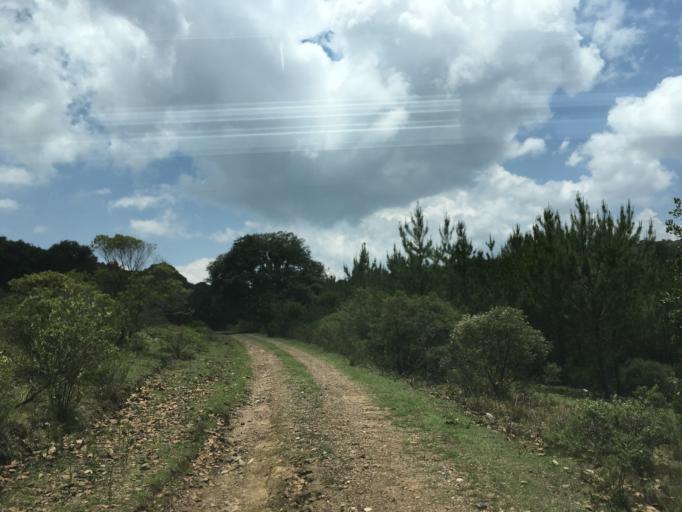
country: MX
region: Oaxaca
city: San Andres Sinaxtla
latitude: 17.6078
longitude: -97.2625
